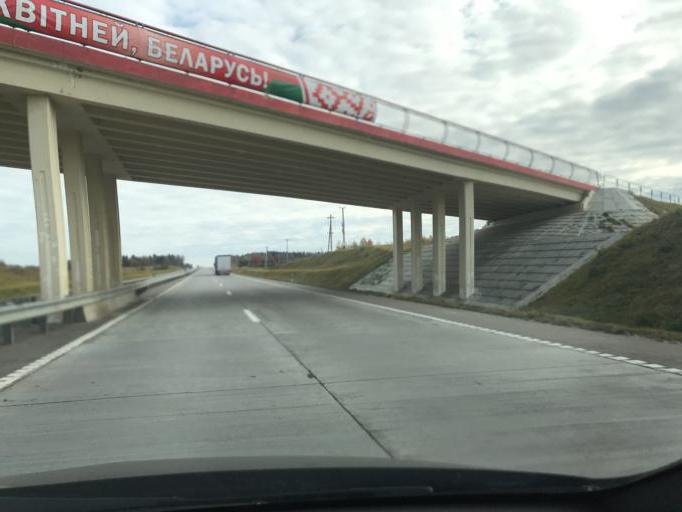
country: BY
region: Minsk
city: Zaslawye
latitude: 54.0637
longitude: 27.3532
